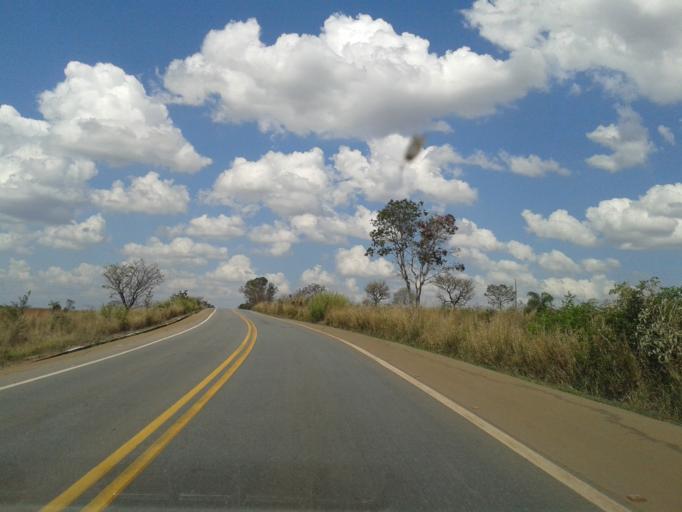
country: BR
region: Minas Gerais
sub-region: Luz
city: Luz
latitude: -19.7729
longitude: -45.7800
